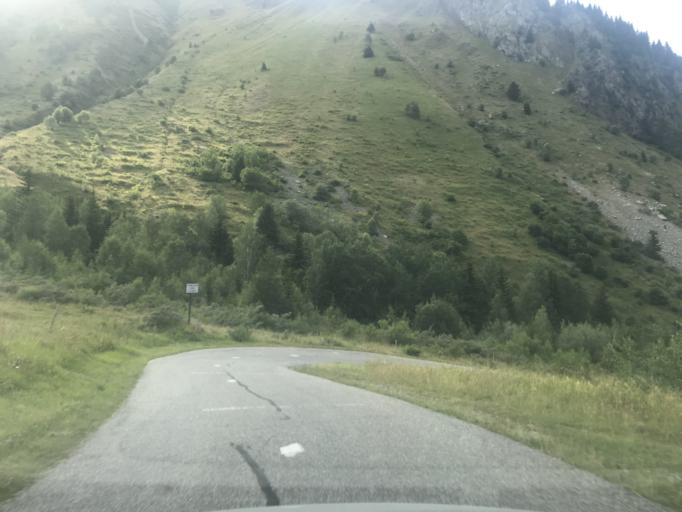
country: FR
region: Rhone-Alpes
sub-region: Departement de la Savoie
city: Saint-Etienne-de-Cuines
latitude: 45.2627
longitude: 6.1961
